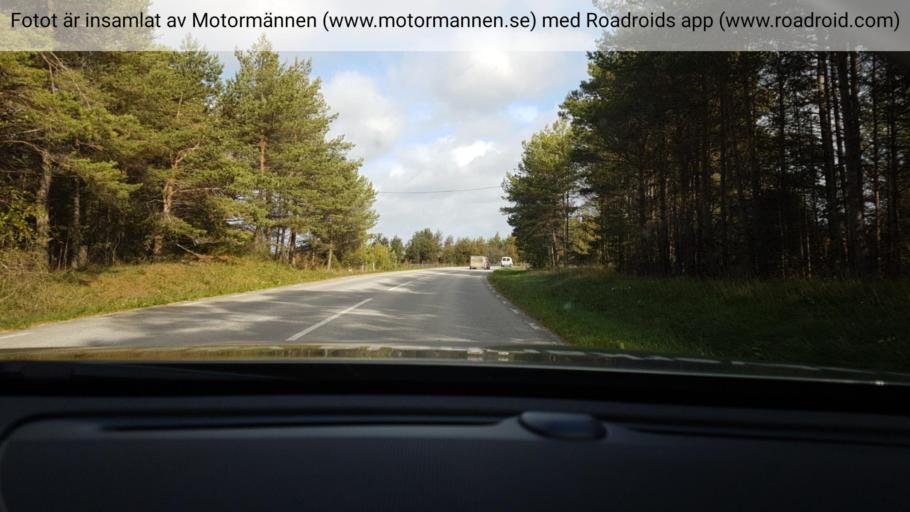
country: SE
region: Gotland
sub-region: Gotland
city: Slite
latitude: 57.8981
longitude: 19.0925
